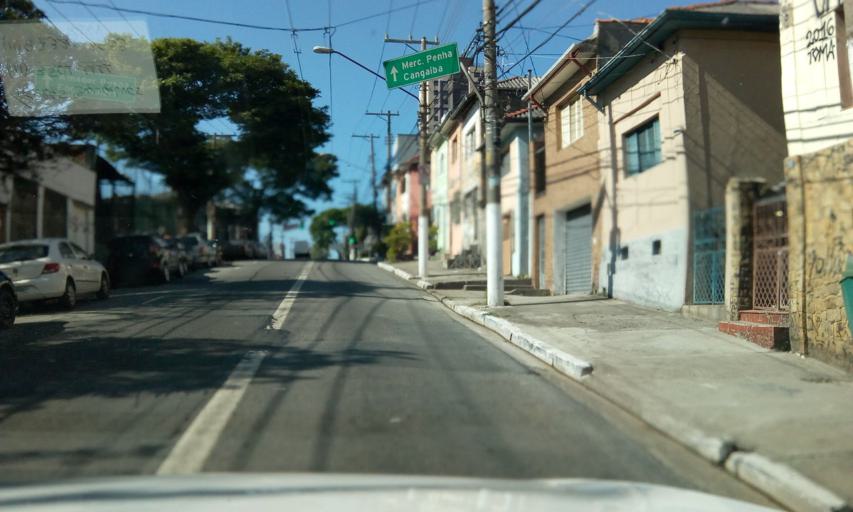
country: BR
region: Sao Paulo
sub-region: Guarulhos
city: Guarulhos
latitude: -23.5252
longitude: -46.5521
